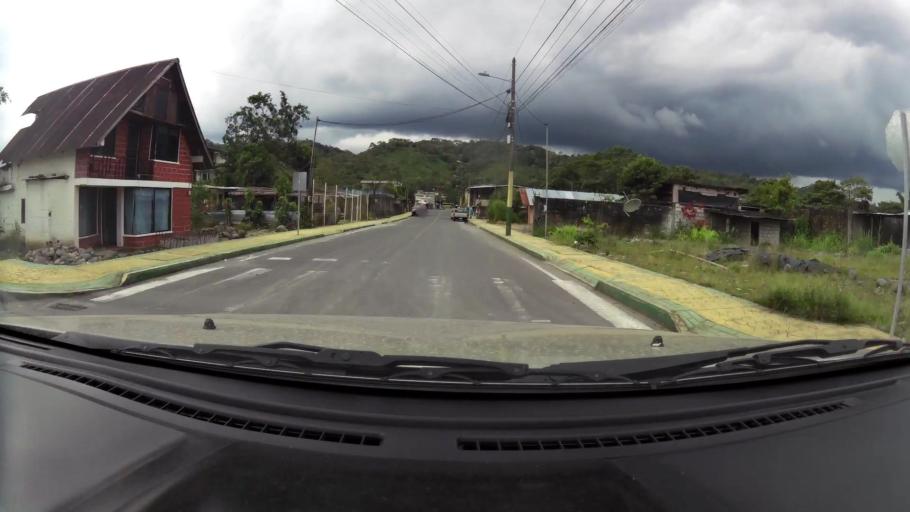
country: EC
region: Pastaza
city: Puyo
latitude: -1.5002
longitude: -78.0196
